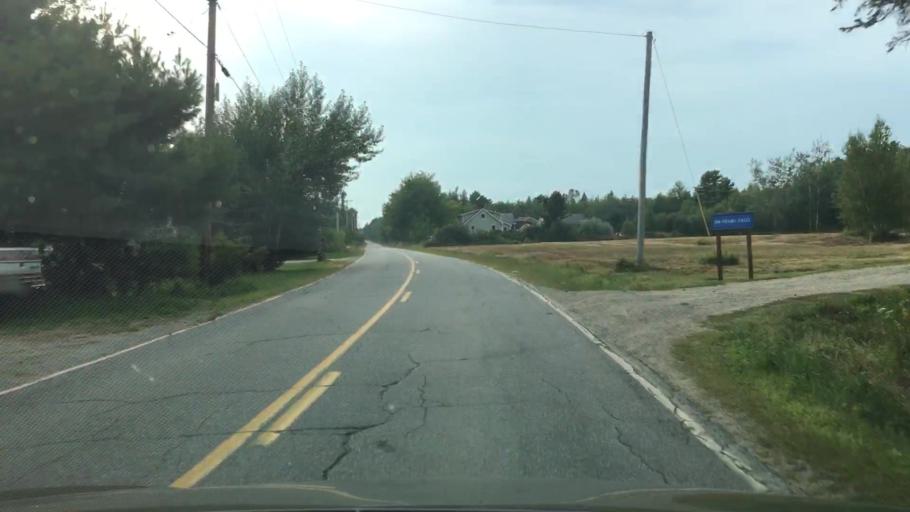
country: US
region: Maine
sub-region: Hancock County
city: Penobscot
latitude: 44.4704
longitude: -68.7438
